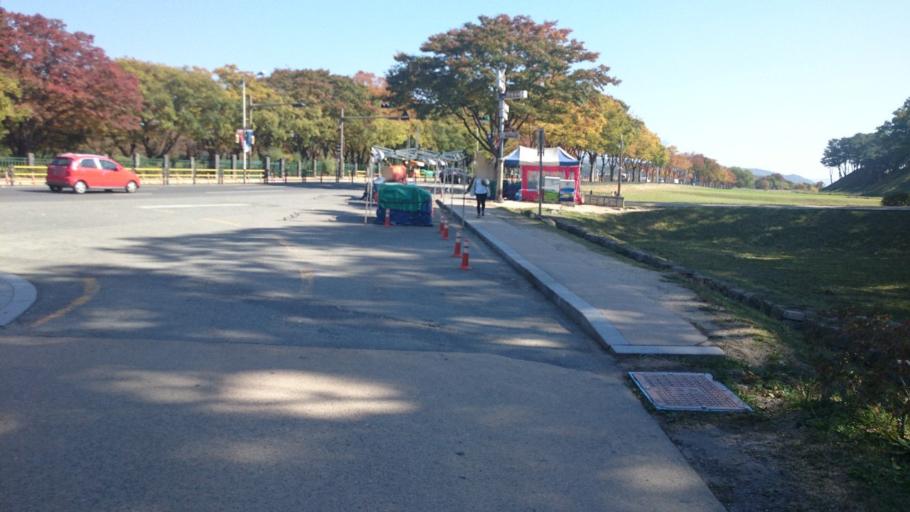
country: KR
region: Gyeongsangbuk-do
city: Kyonju
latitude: 35.8338
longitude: 129.2248
